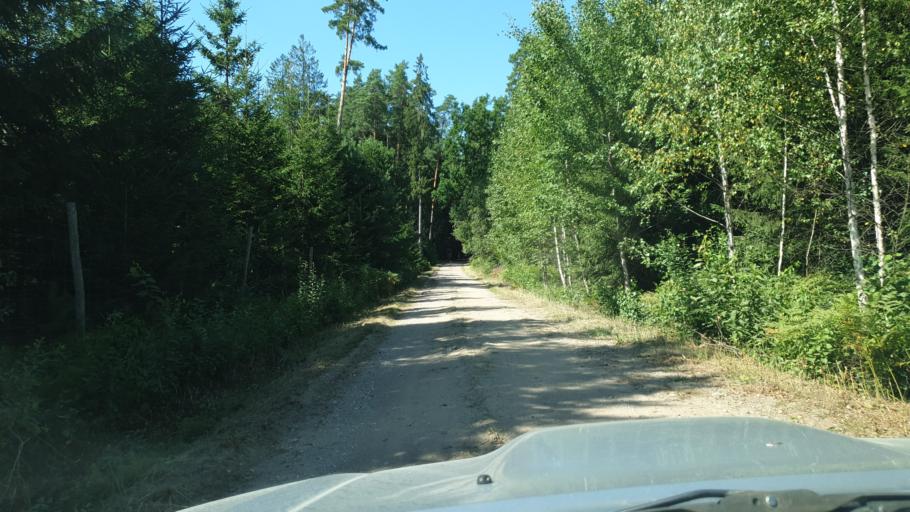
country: LT
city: Sirvintos
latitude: 54.9077
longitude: 24.9412
